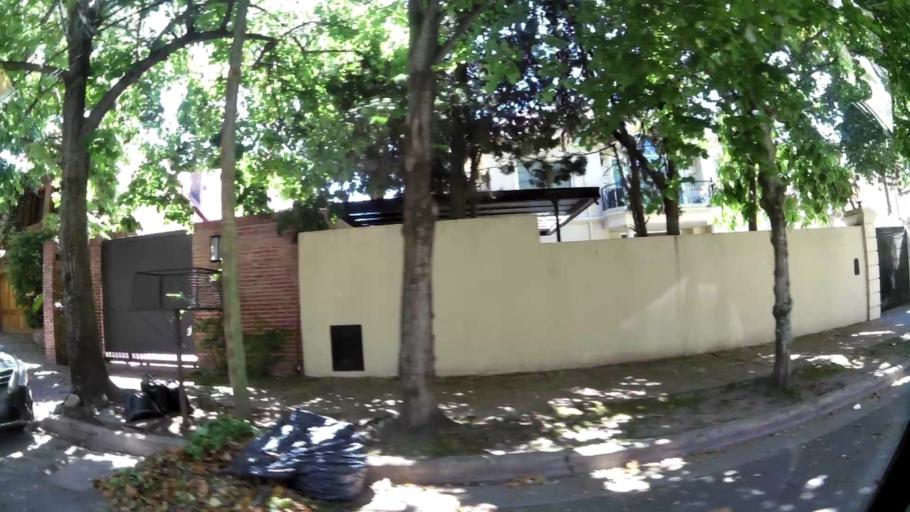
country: AR
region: Buenos Aires
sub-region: Partido de San Isidro
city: San Isidro
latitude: -34.4800
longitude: -58.4884
